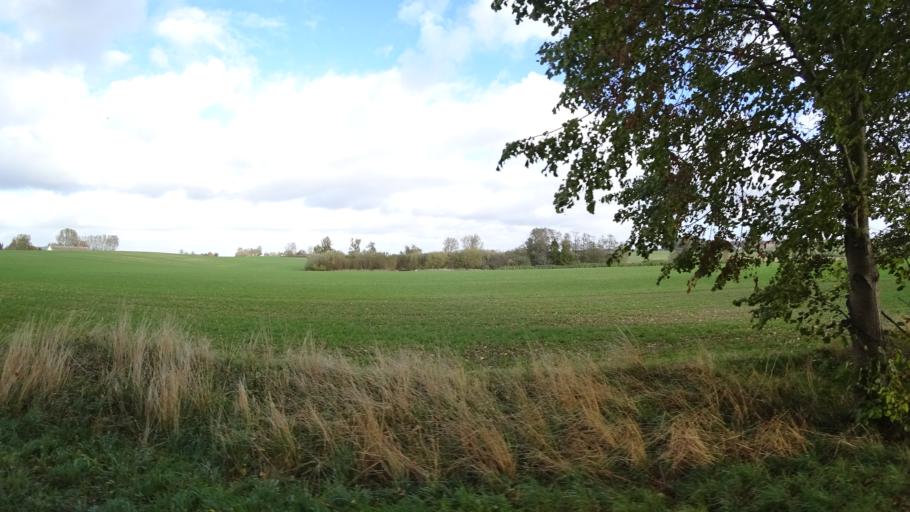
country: SE
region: Skane
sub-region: Staffanstorps Kommun
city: Staffanstorp
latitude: 55.6145
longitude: 13.2053
